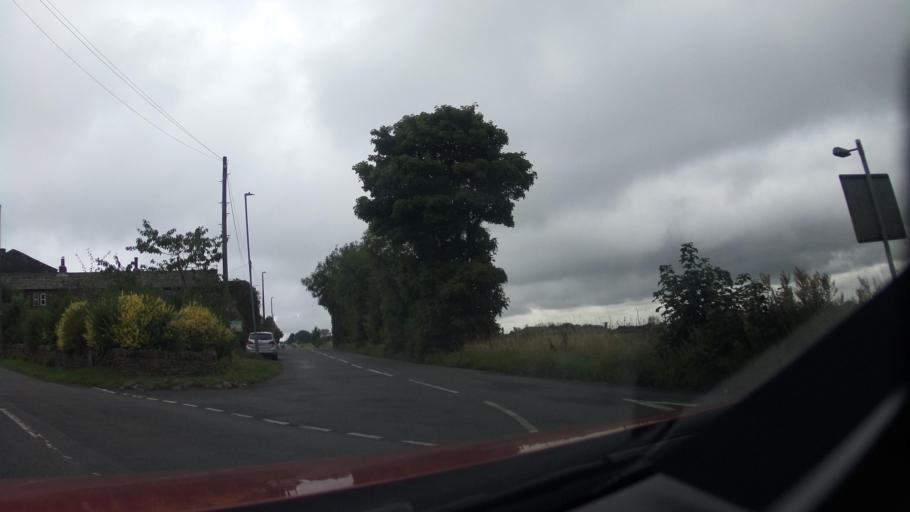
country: GB
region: England
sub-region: Kirklees
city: Shelley
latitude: 53.6146
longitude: -1.6536
